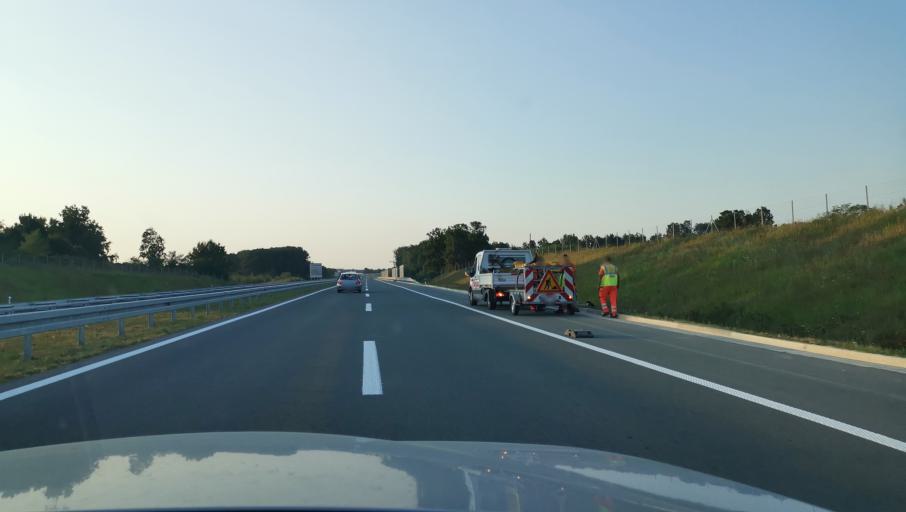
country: RS
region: Central Serbia
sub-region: Kolubarski Okrug
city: Lajkovac
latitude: 44.3685
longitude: 20.1196
